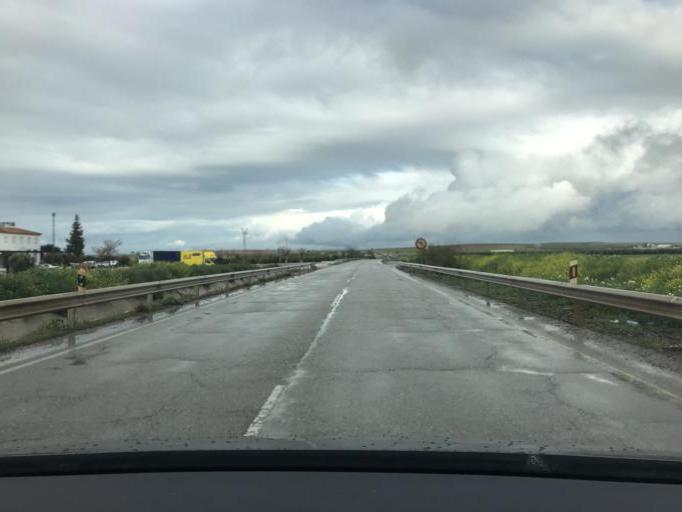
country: ES
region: Andalusia
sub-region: Provincia de Sevilla
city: La Luisiana
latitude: 37.4868
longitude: -5.1723
